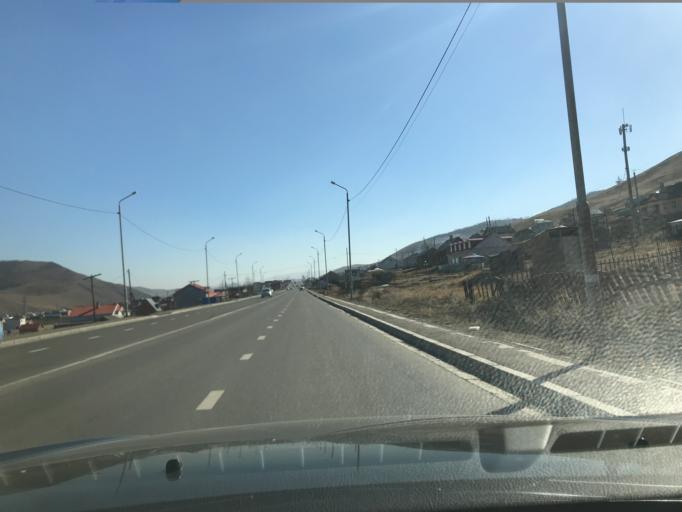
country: MN
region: Ulaanbaatar
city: Ulaanbaatar
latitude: 48.0463
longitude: 106.9015
